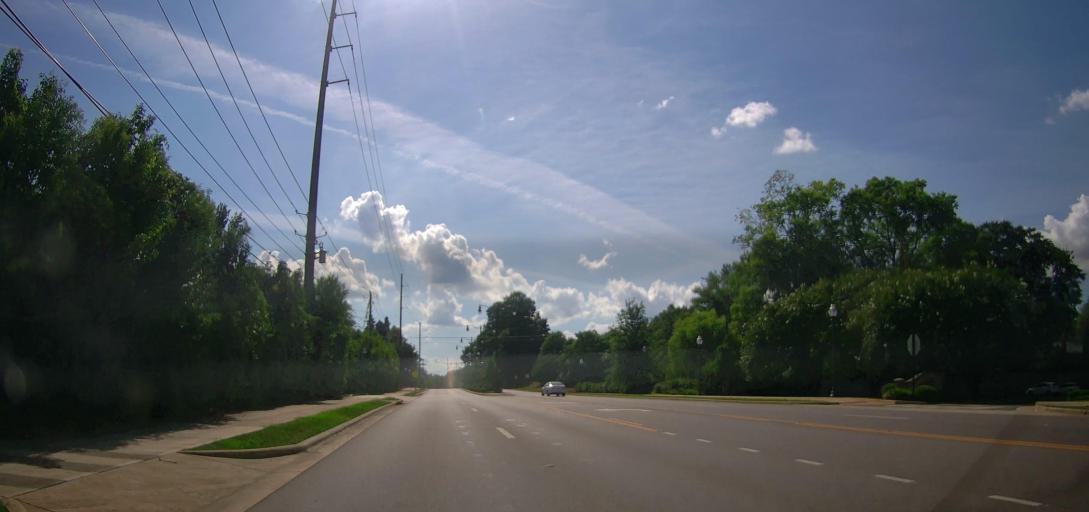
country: US
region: Alabama
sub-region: Tuscaloosa County
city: Holt
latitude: 33.2060
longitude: -87.5189
